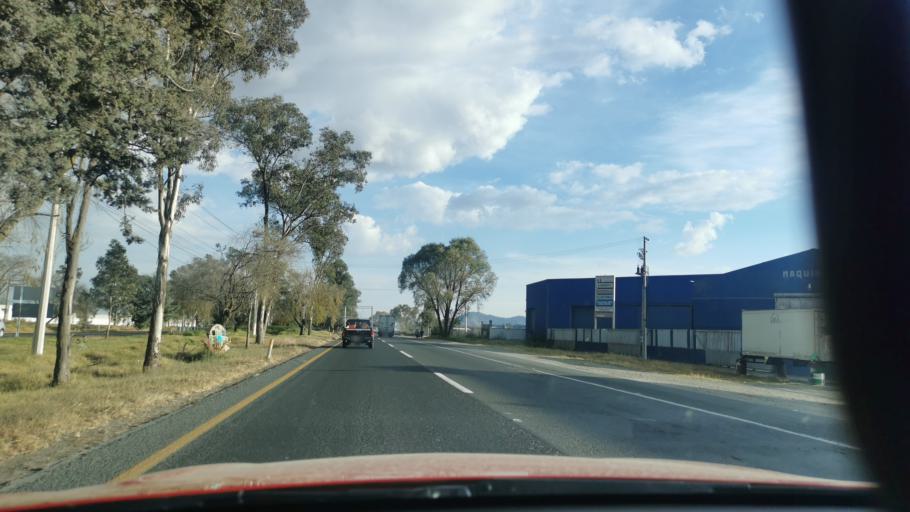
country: MX
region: Mexico
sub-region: Toluca
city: Colonia Aviacion Autopan
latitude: 19.3738
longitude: -99.6987
